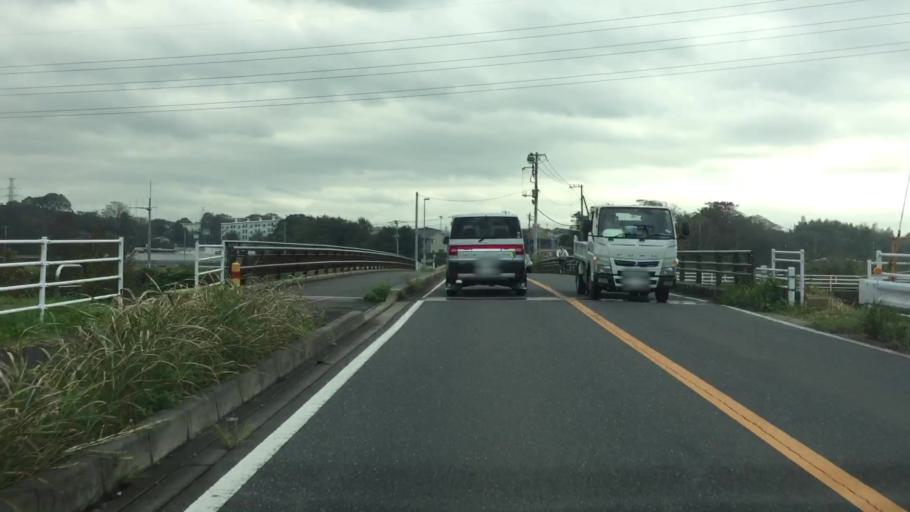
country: JP
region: Chiba
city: Kashiwa
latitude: 35.8473
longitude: 139.9905
